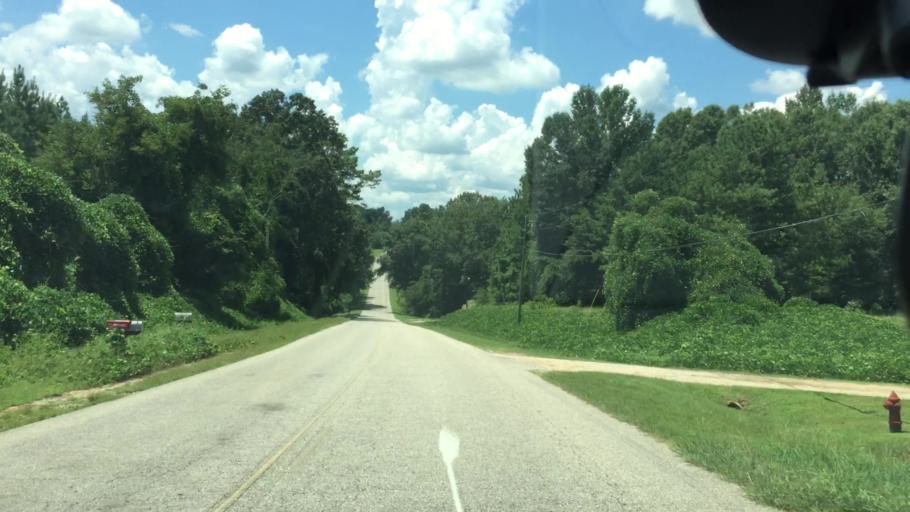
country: US
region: Alabama
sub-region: Pike County
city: Troy
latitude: 31.7498
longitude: -85.9778
